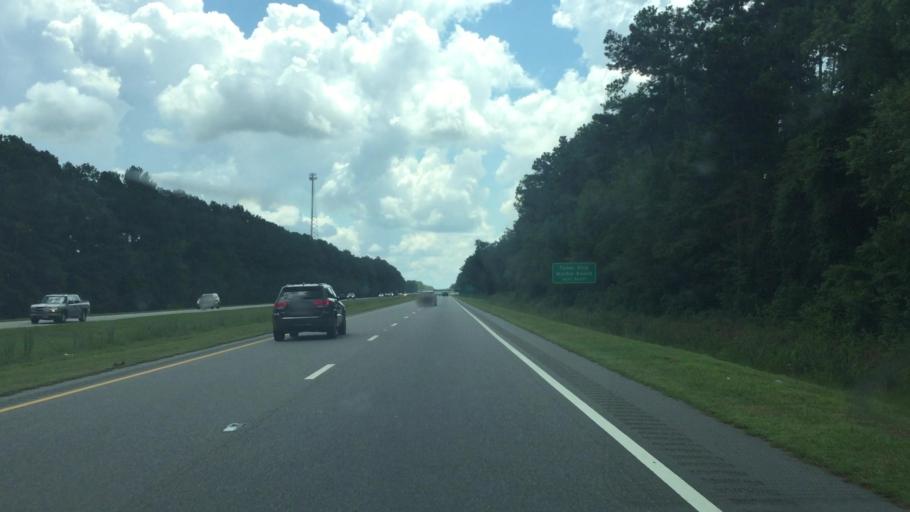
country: US
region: North Carolina
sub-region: Columbus County
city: Chadbourn
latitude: 34.3716
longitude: -78.8427
